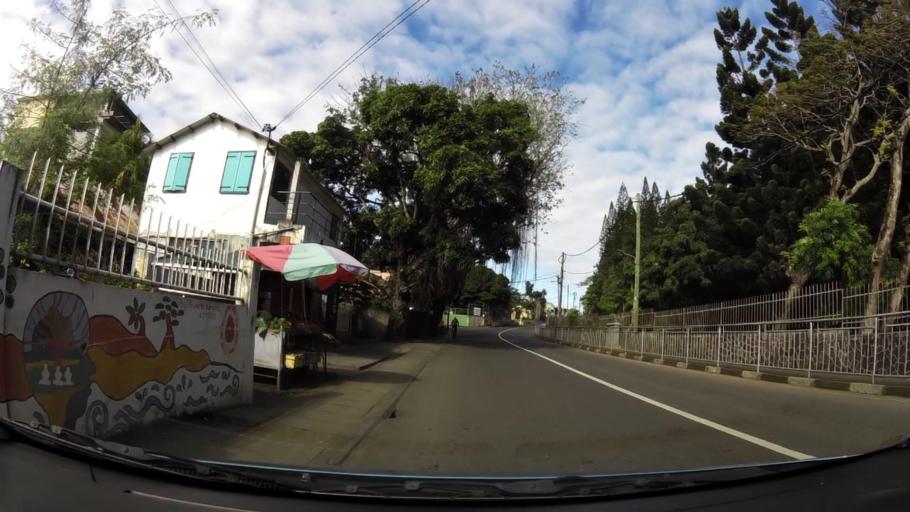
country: MU
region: Grand Port
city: Mahebourg
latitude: -20.4163
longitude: 57.7049
